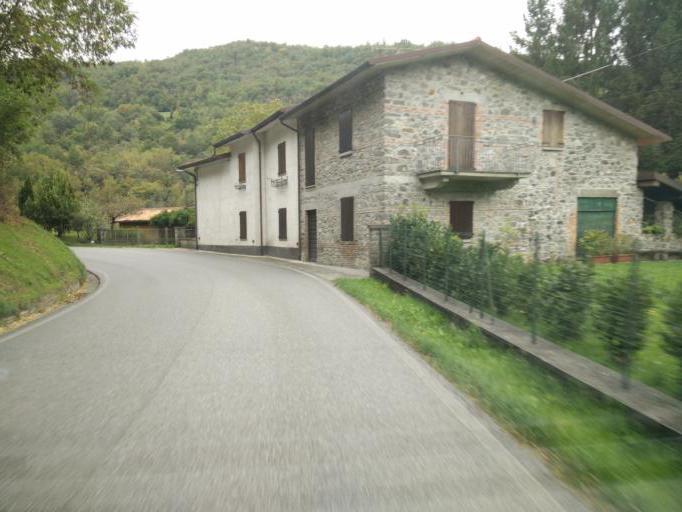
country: IT
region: Tuscany
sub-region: Provincia di Massa-Carrara
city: Fivizzano
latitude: 44.1940
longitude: 10.1298
